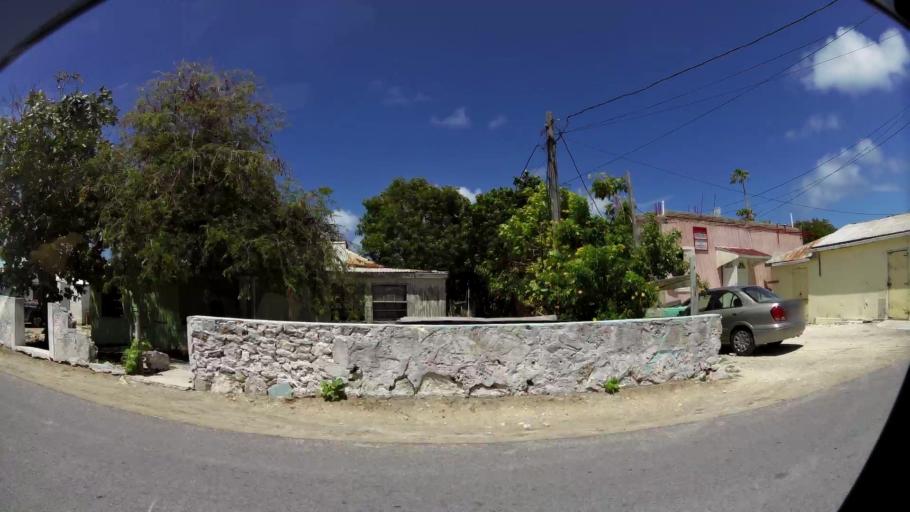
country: TC
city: Cockburn Town
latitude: 21.4738
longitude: -71.1464
